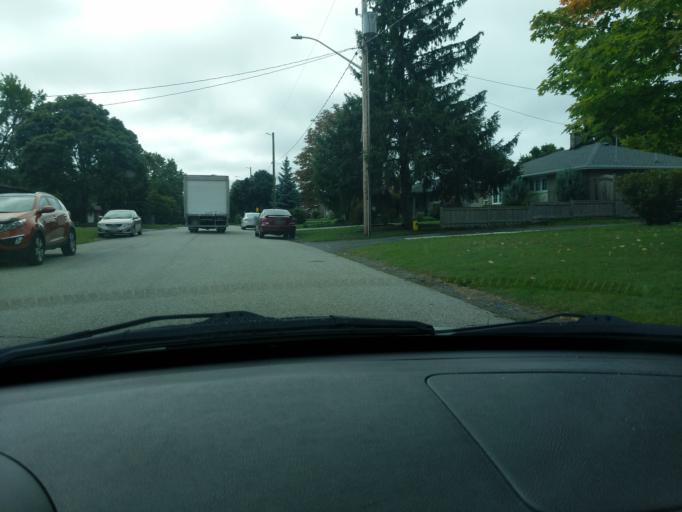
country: CA
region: Ontario
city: Cambridge
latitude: 43.4214
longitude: -80.3164
